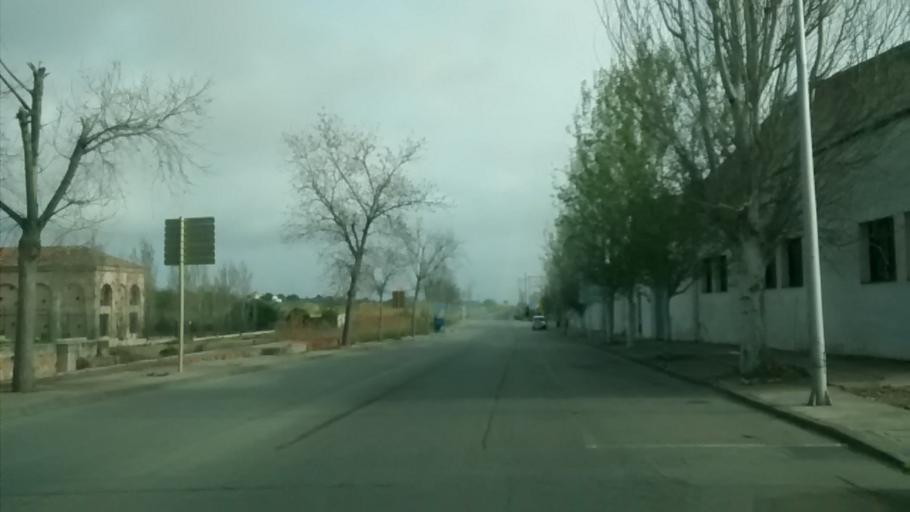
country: ES
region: Catalonia
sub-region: Provincia de Tarragona
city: Sant Carles de la Rapita
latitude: 40.6208
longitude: 0.5988
